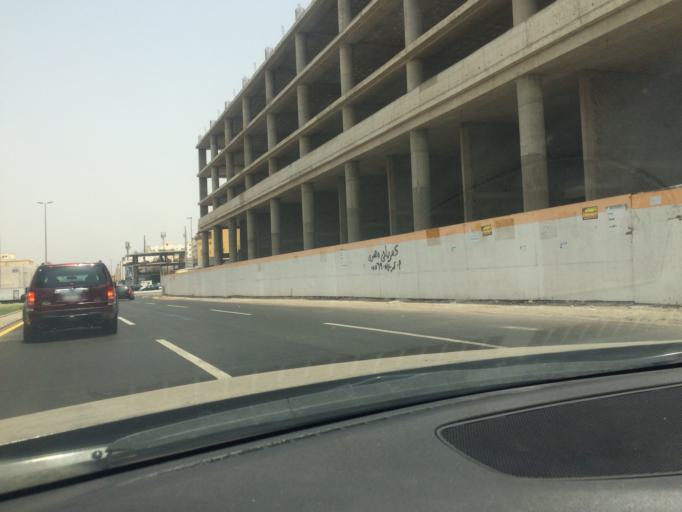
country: SA
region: Makkah
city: Jeddah
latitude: 21.6058
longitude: 39.1195
